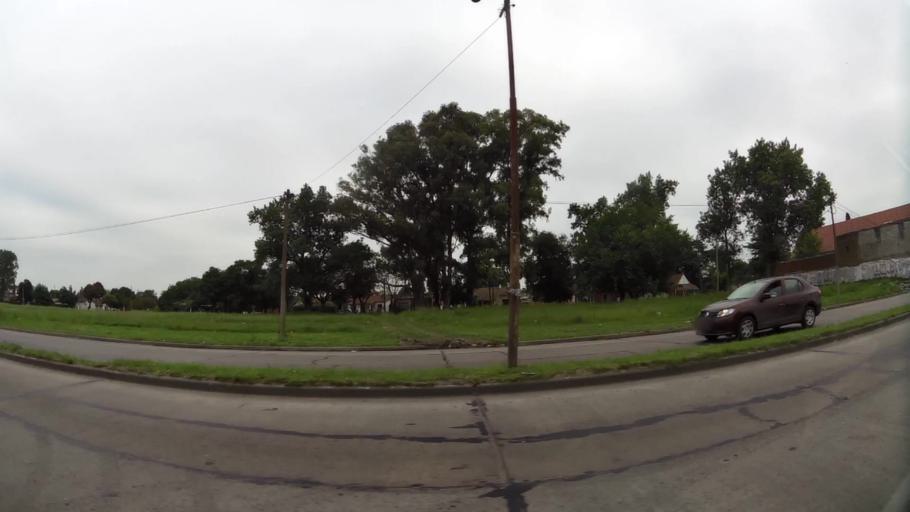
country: AR
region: Buenos Aires
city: San Justo
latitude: -34.7063
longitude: -58.5487
